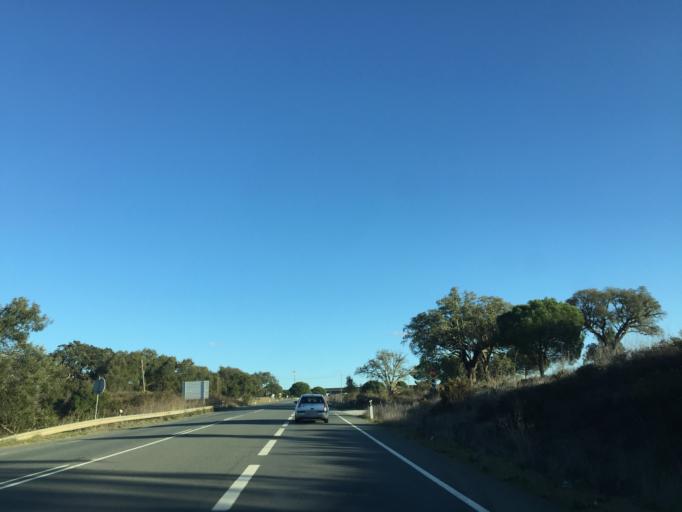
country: PT
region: Setubal
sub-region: Grandola
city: Grandola
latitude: 38.1194
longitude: -8.4246
